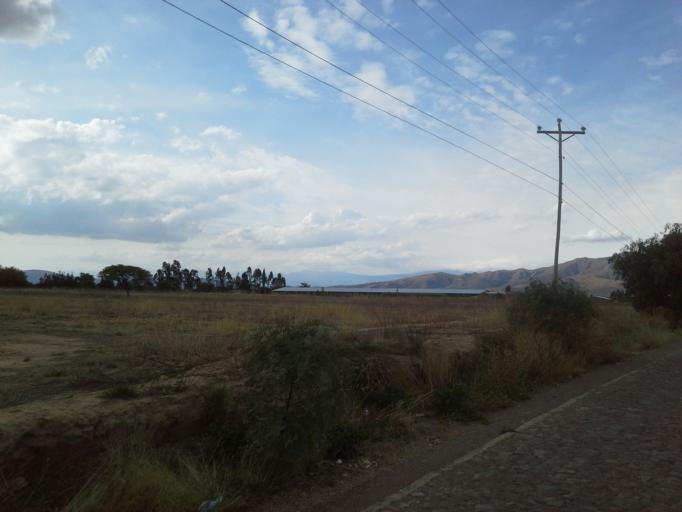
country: BO
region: Cochabamba
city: Tarata
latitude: -17.5940
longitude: -66.0186
